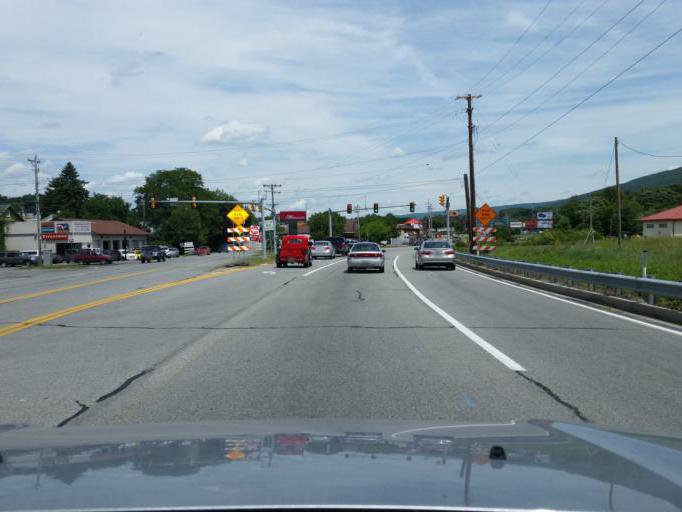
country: US
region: Pennsylvania
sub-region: Blair County
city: Altoona
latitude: 40.4964
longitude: -78.3942
